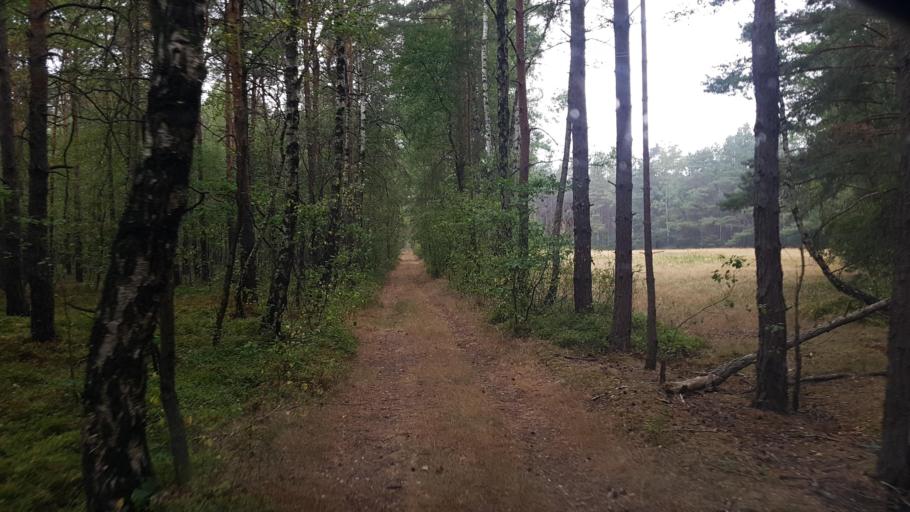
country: DE
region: Brandenburg
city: Sallgast
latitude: 51.6038
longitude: 13.8273
